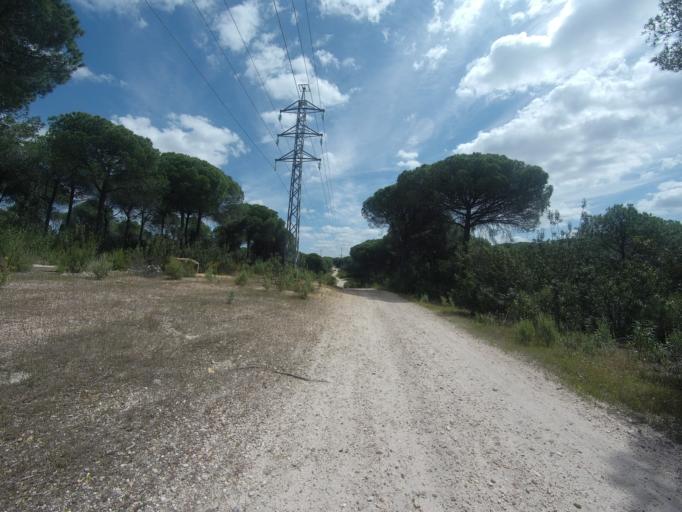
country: ES
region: Andalusia
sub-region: Provincia de Huelva
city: Aljaraque
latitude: 37.2249
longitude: -7.0640
